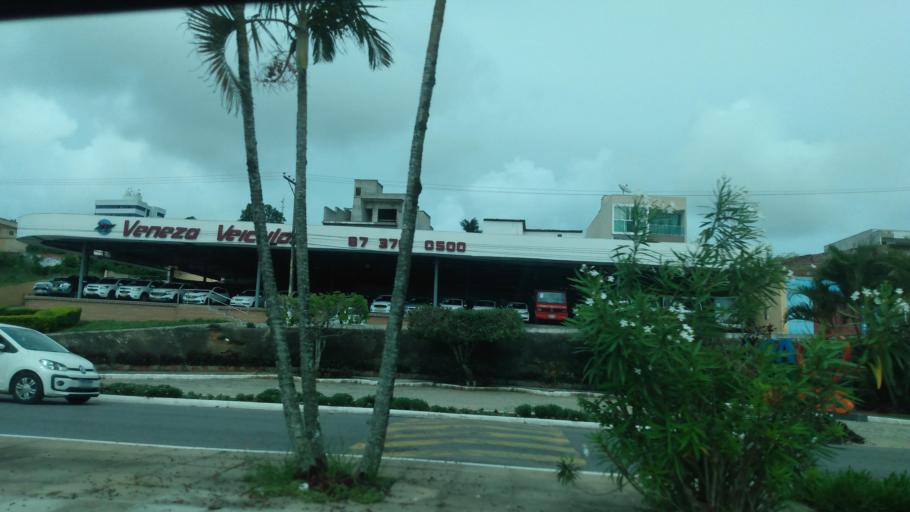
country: BR
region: Pernambuco
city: Garanhuns
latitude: -8.8774
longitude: -36.4747
